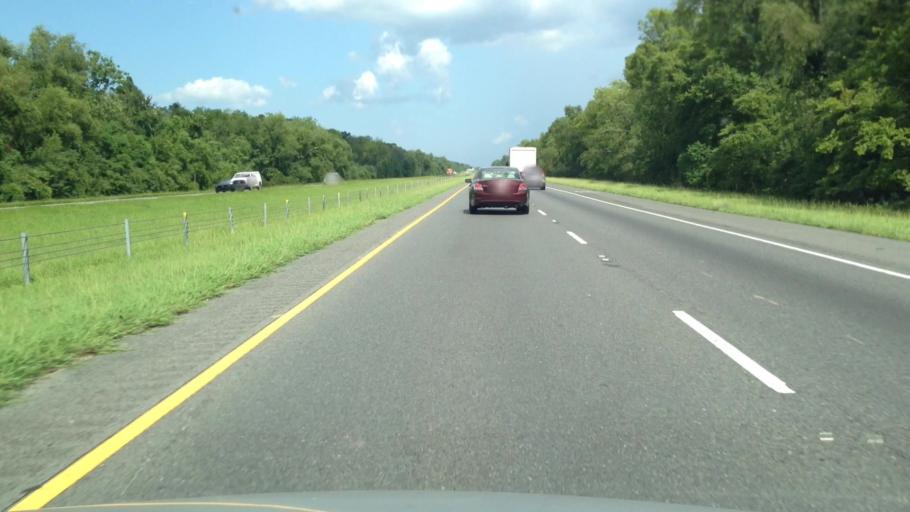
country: US
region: Louisiana
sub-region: Saint James Parish
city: Grand Point
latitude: 30.1360
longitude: -90.7346
